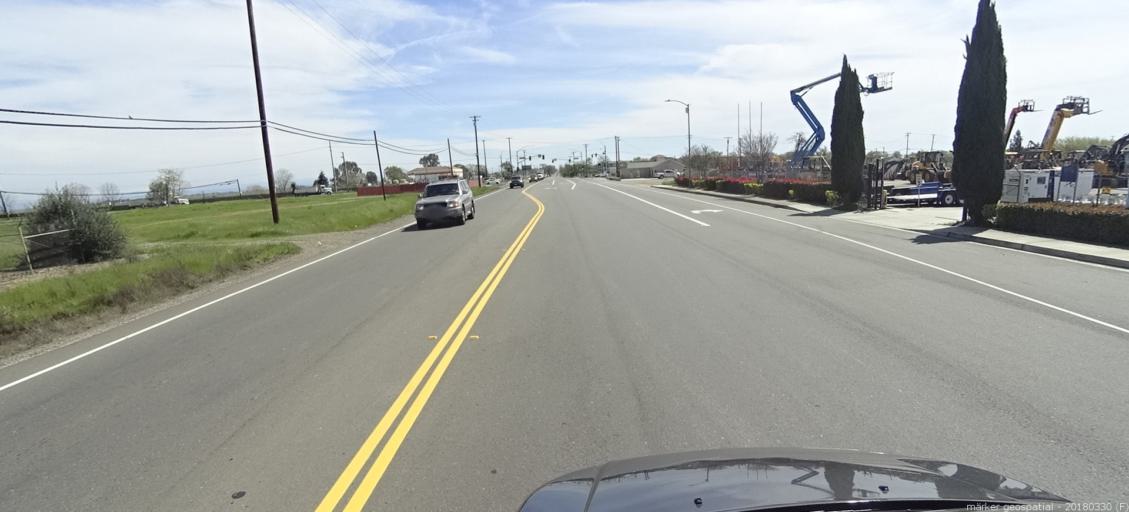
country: US
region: California
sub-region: Sacramento County
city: Rosemont
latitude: 38.5295
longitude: -121.3370
